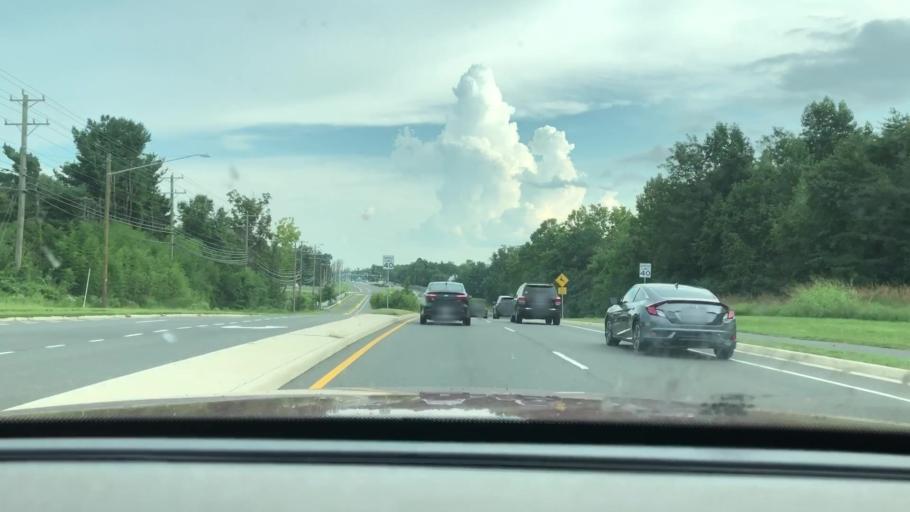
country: US
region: Virginia
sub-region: Fairfax County
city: Greenbriar
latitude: 38.8702
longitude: -77.4079
